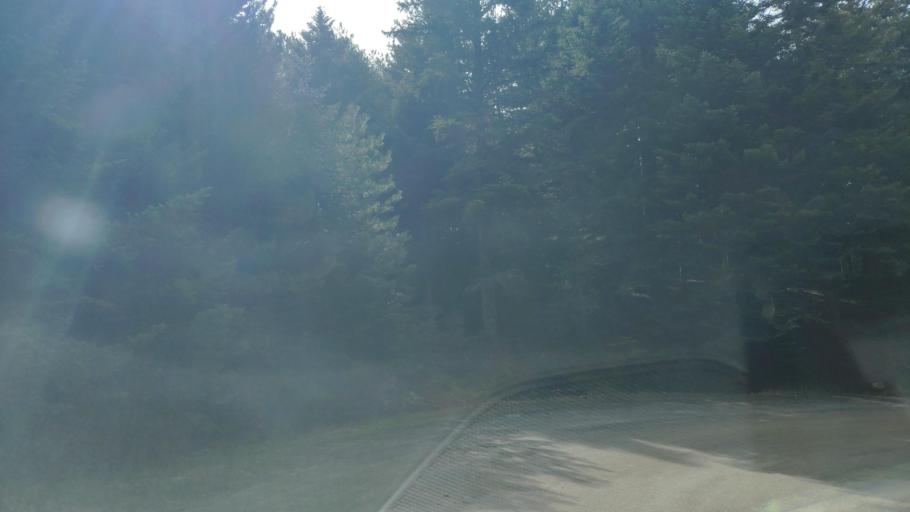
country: GR
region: West Greece
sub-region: Nomos Achaias
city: Aiyira
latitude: 38.0243
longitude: 22.3904
